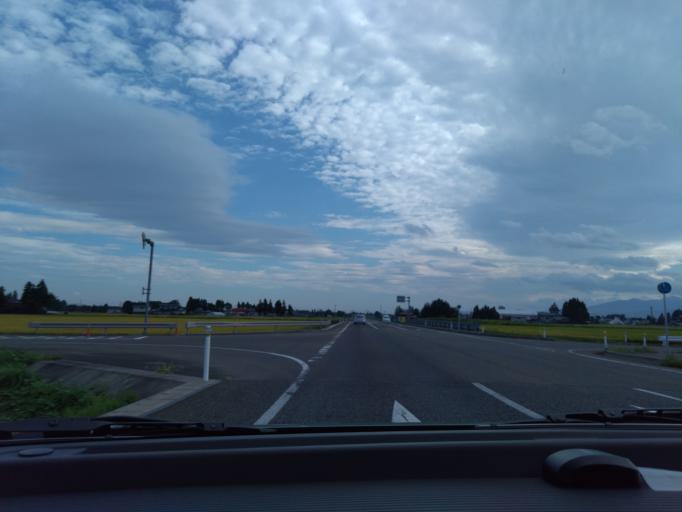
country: JP
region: Iwate
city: Hanamaki
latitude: 39.3695
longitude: 141.0568
